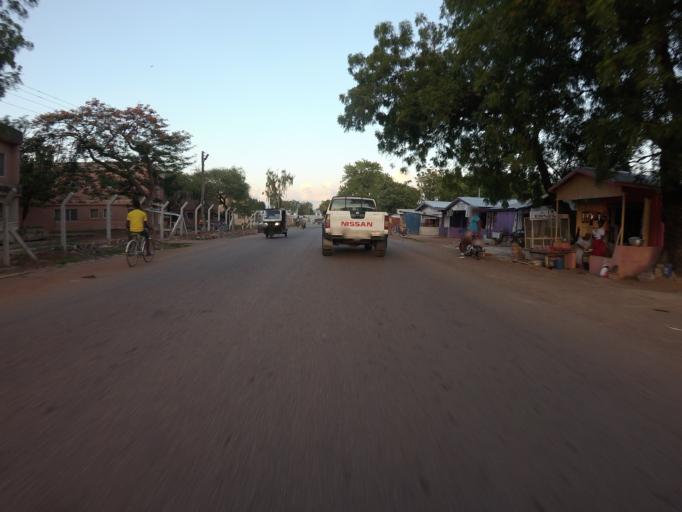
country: GH
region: Upper East
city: Navrongo
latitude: 10.8967
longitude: -1.0872
